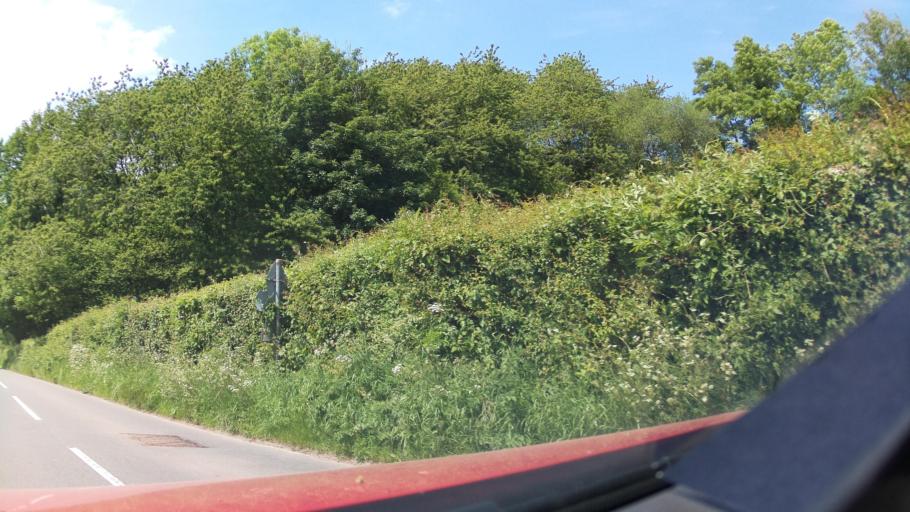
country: GB
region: England
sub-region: Herefordshire
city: Llanrothal
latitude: 51.8449
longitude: -2.7818
